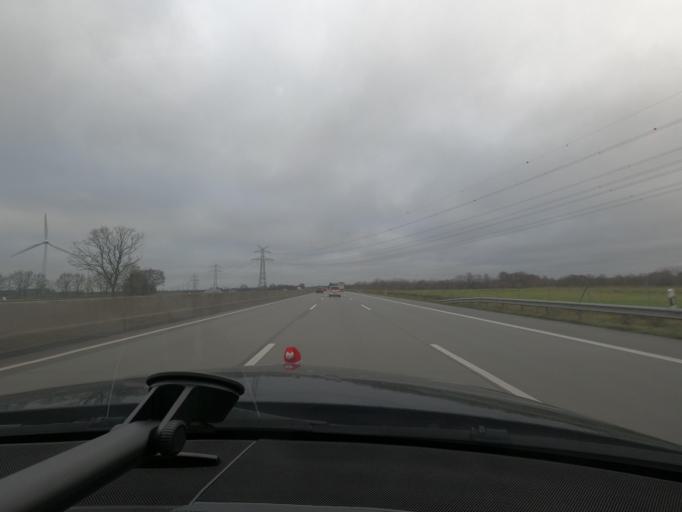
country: DE
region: Schleswig-Holstein
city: Bimohlen
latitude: 53.9551
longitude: 9.9505
